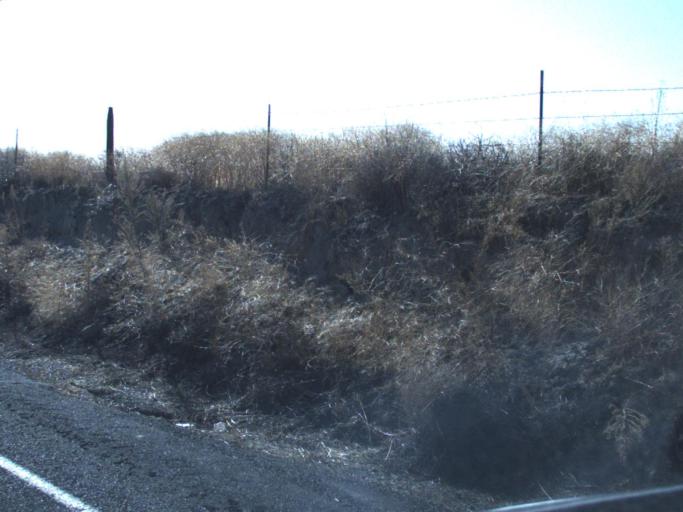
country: US
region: Washington
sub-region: Adams County
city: Ritzville
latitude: 47.0647
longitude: -118.6630
